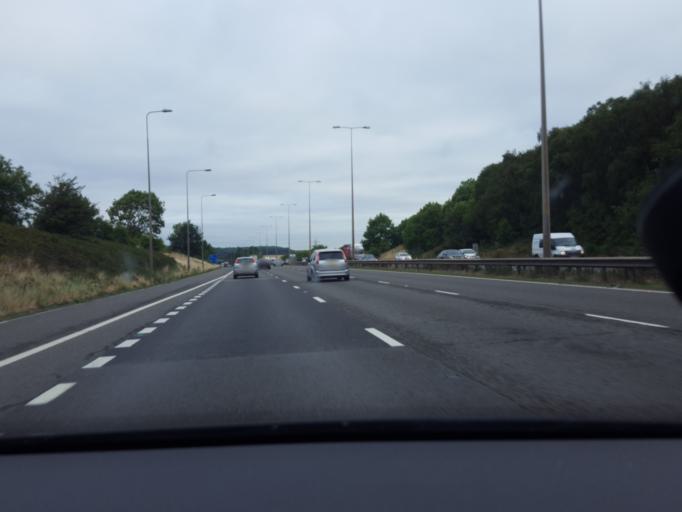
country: GB
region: England
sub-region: Leicestershire
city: Shepshed
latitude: 52.7662
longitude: -1.2749
